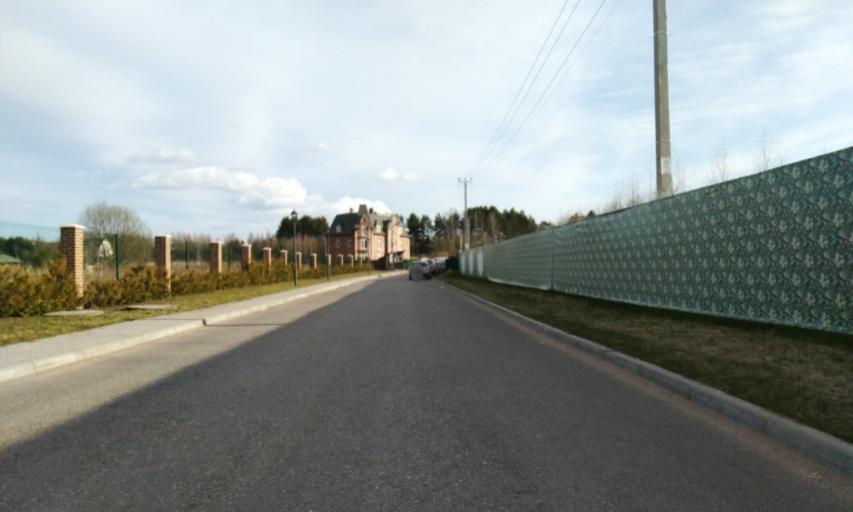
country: RU
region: Leningrad
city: Novoye Devyatkino
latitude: 60.1101
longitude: 30.4462
